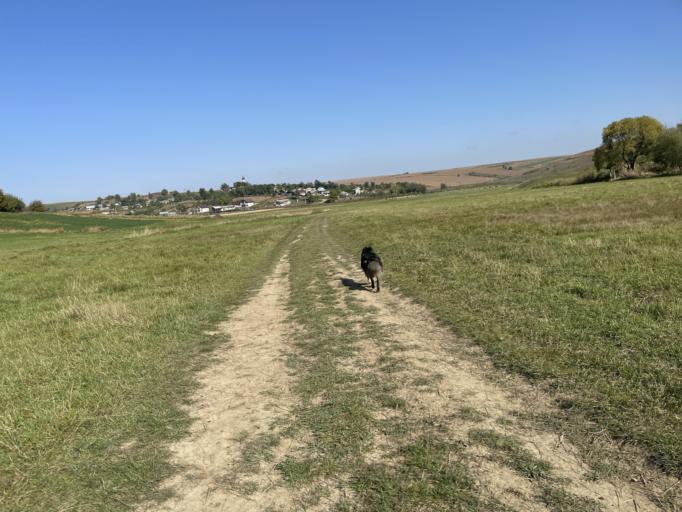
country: RO
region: Iasi
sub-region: Comuna Dumesti
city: Pausesti
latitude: 47.1572
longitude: 27.3089
